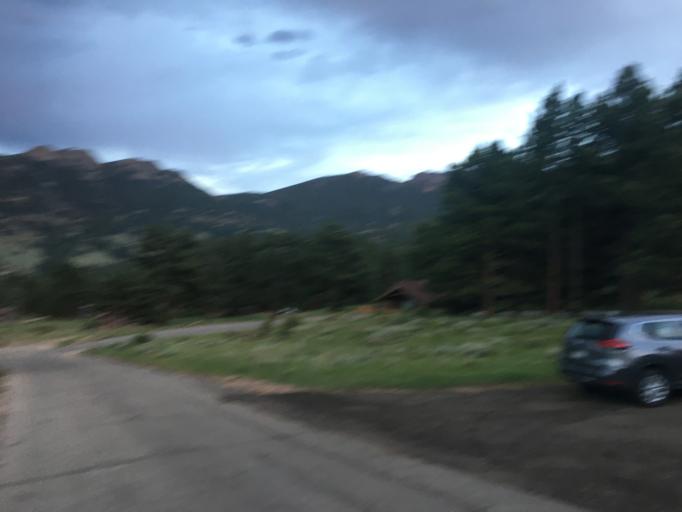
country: US
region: Colorado
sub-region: Larimer County
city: Estes Park
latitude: 40.3369
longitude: -105.5779
